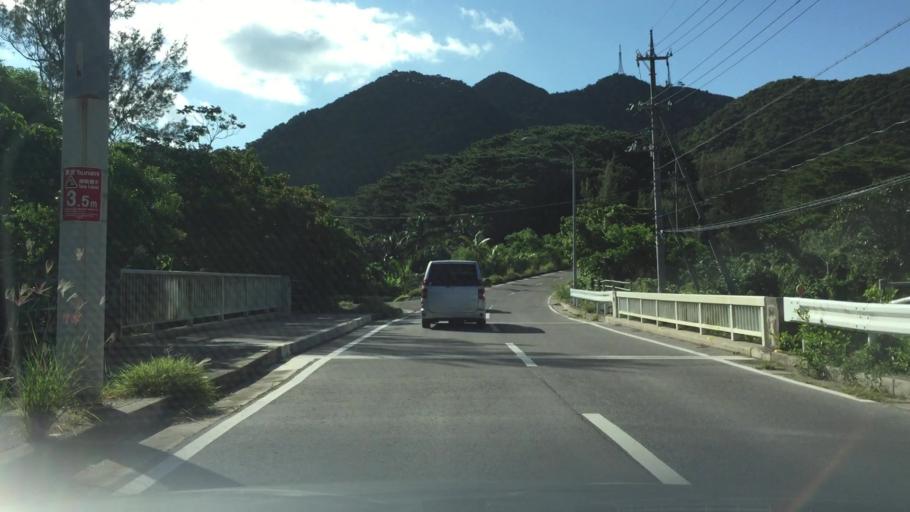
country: JP
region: Okinawa
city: Ishigaki
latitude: 24.4464
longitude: 124.1343
